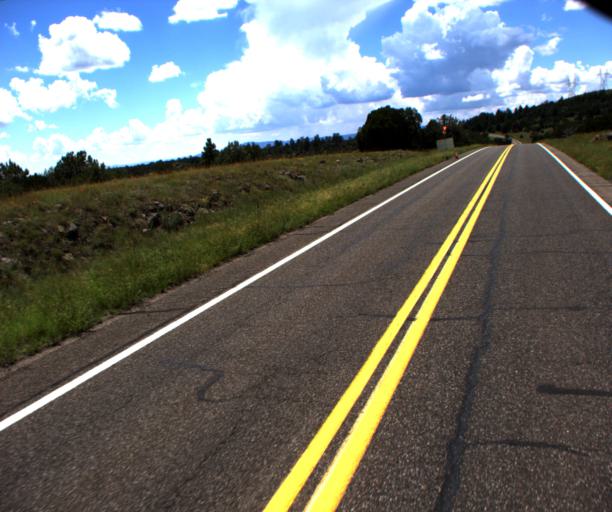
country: US
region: Arizona
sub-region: Gila County
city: Pine
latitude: 34.5158
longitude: -111.5328
